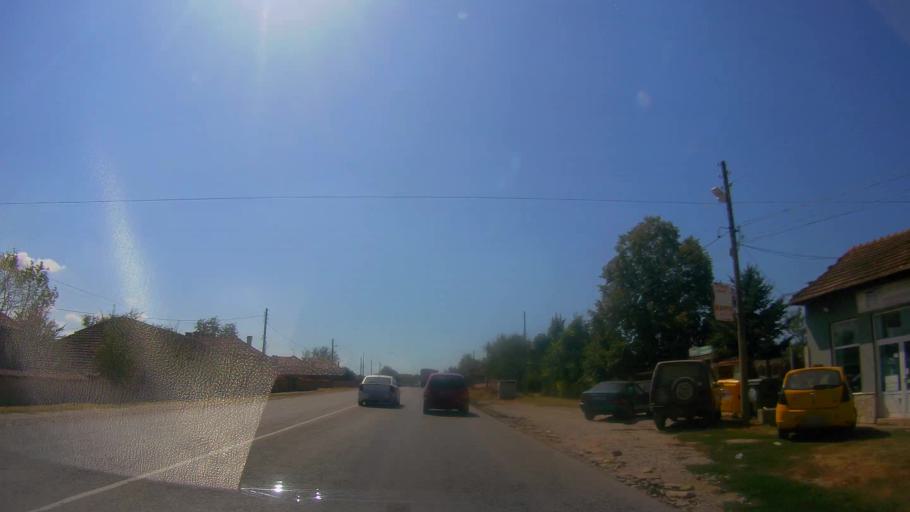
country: BG
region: Veliko Turnovo
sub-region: Obshtina Gorna Oryakhovitsa
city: Purvomaytsi
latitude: 43.2636
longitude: 25.6423
